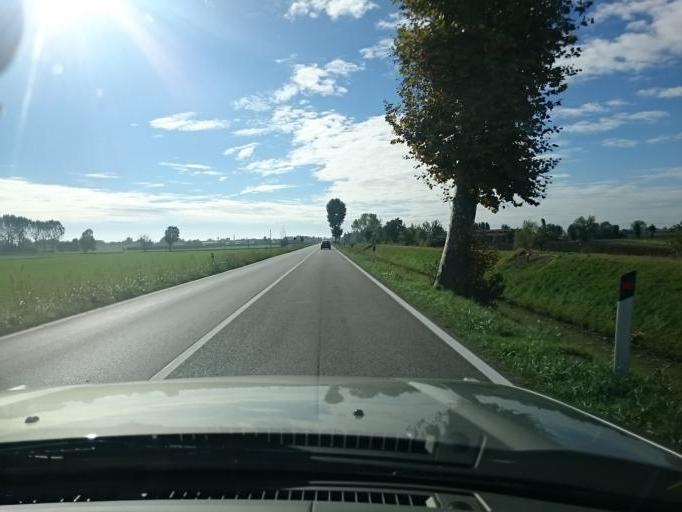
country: IT
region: Veneto
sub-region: Provincia di Padova
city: Bovolenta
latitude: 45.2869
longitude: 11.9268
